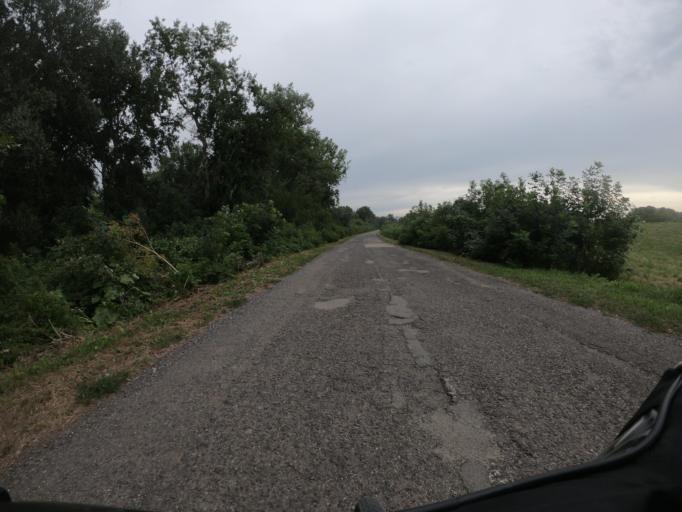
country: HU
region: Hajdu-Bihar
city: Tiszacsege
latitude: 47.7217
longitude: 20.9515
